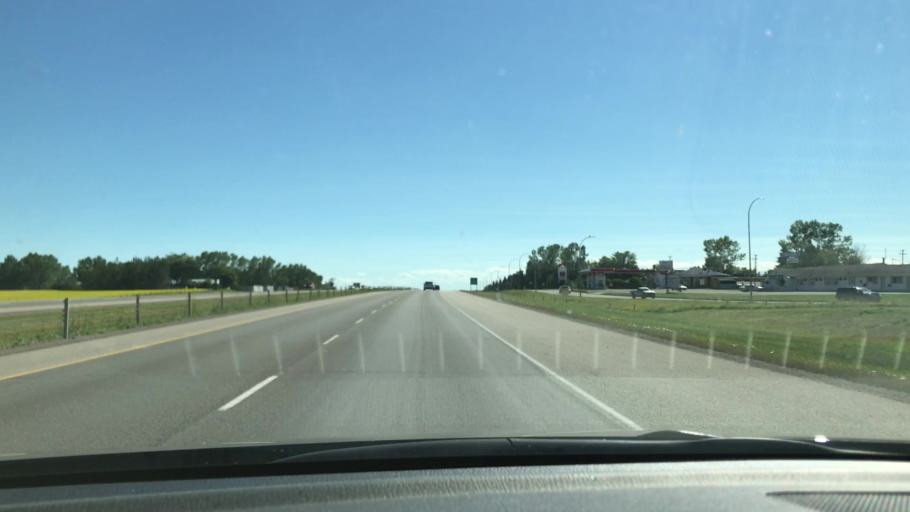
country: CA
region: Alberta
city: Penhold
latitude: 52.0167
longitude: -113.9440
